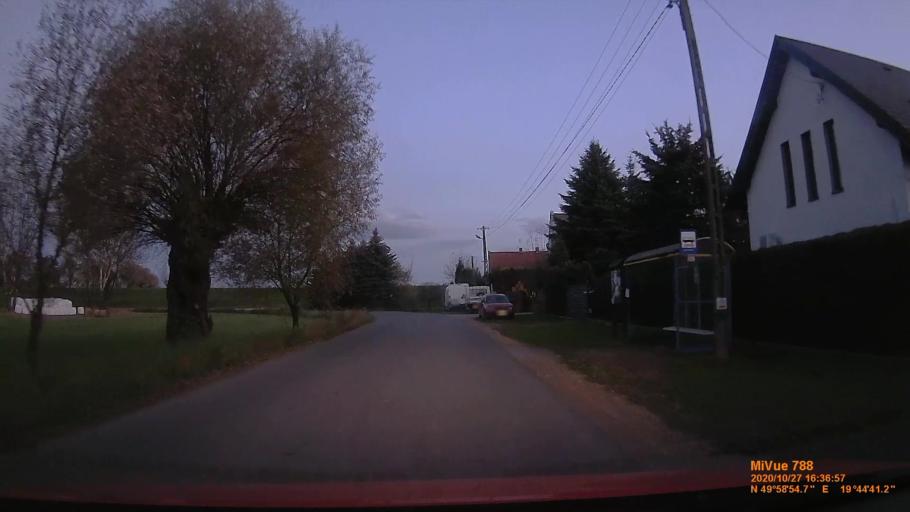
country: PL
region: Lesser Poland Voivodeship
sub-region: Powiat krakowski
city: Wolowice
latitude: 49.9819
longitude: 19.7448
